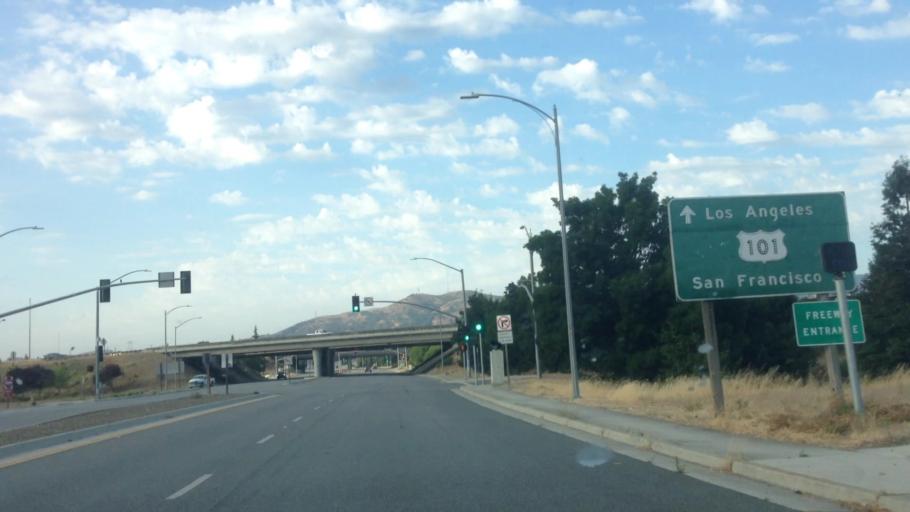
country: US
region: California
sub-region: Santa Clara County
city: Seven Trees
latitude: 37.2458
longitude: -121.7730
